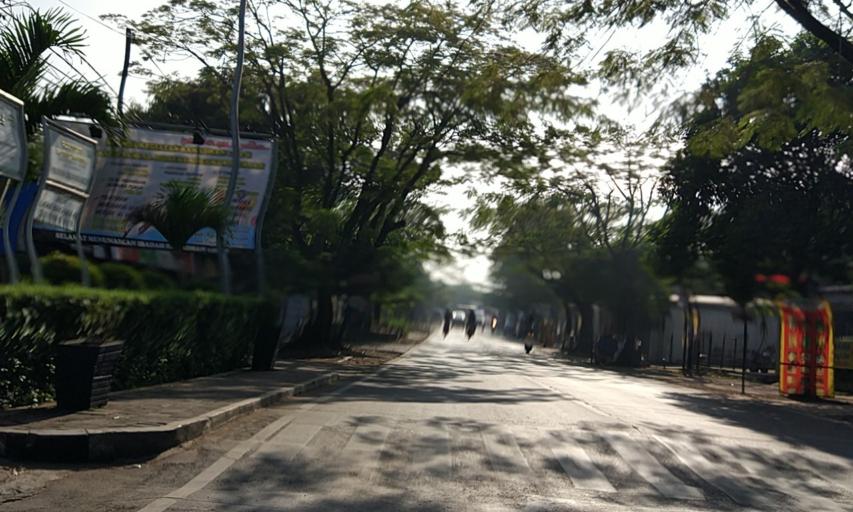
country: ID
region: West Java
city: Bandung
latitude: -6.9180
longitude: 107.6750
